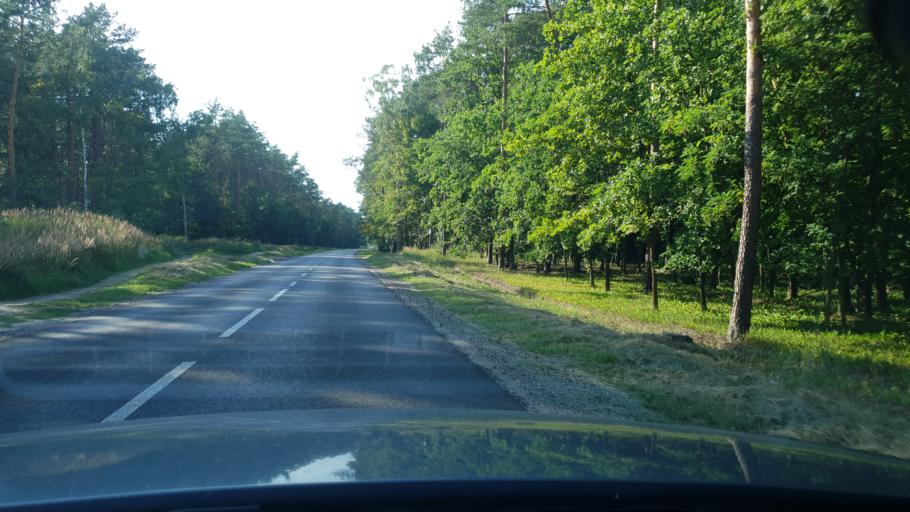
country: PL
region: Kujawsko-Pomorskie
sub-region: Grudziadz
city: Grudziadz
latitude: 53.4469
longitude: 18.7423
